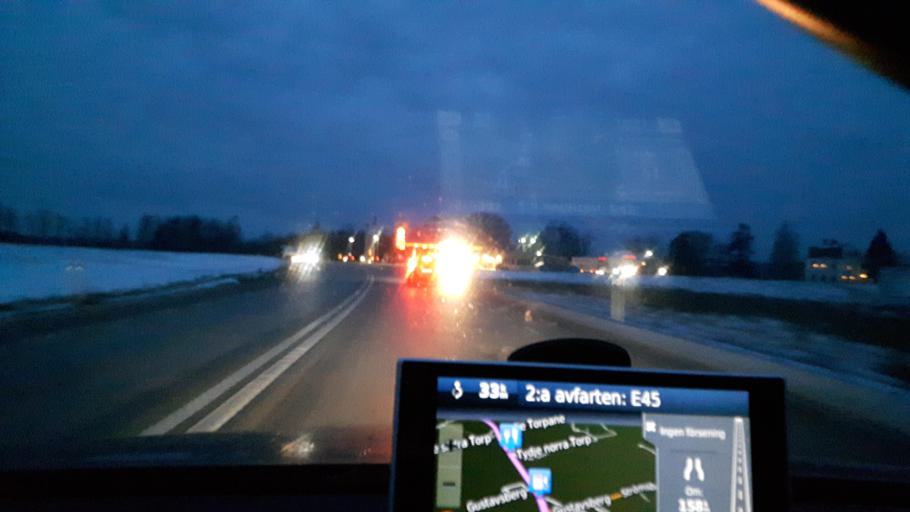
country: SE
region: Vaestra Goetaland
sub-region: Amals Kommun
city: Amal
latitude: 58.9746
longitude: 12.6256
